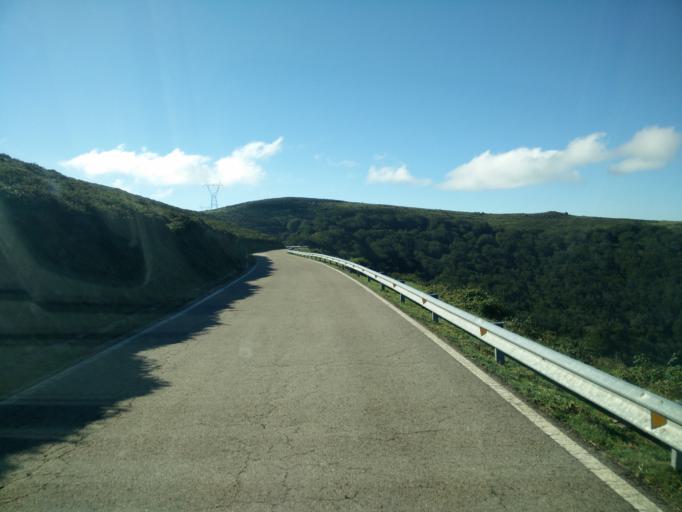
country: ES
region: Cantabria
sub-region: Provincia de Cantabria
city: San Pedro del Romeral
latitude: 43.0455
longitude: -3.8512
